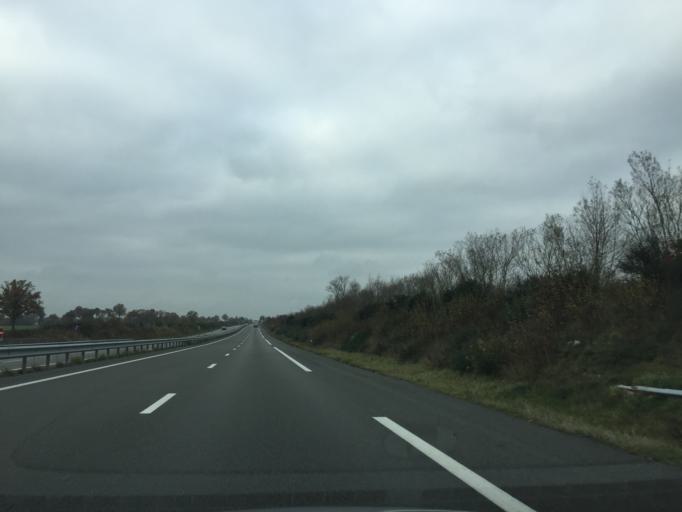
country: FR
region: Limousin
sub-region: Departement de la Creuse
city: Gouzon
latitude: 46.2055
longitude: 2.2675
